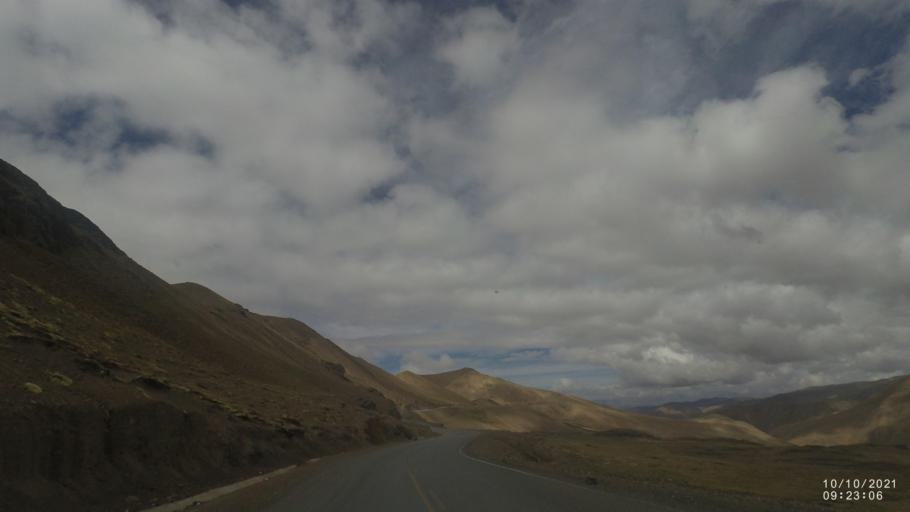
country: BO
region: La Paz
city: Quime
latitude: -17.0822
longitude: -67.3004
